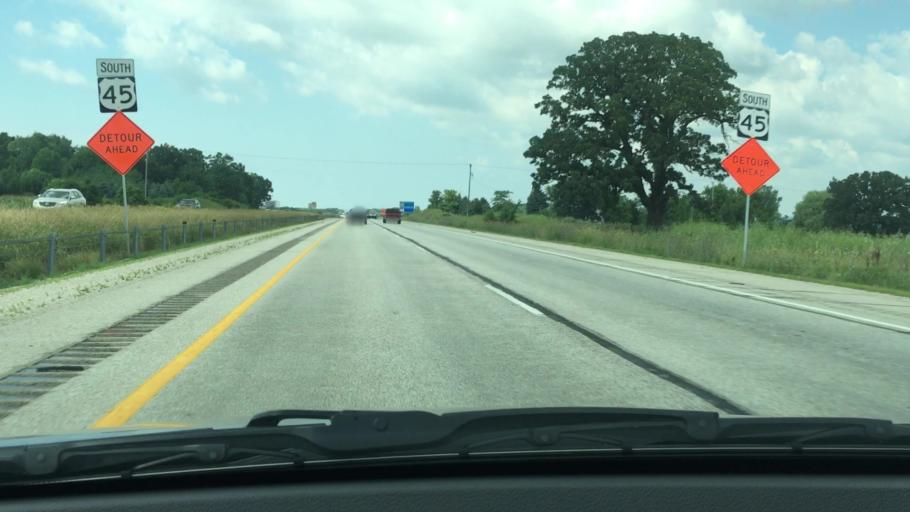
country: US
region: Wisconsin
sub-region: Dodge County
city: Lomira
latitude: 43.6734
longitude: -88.4417
